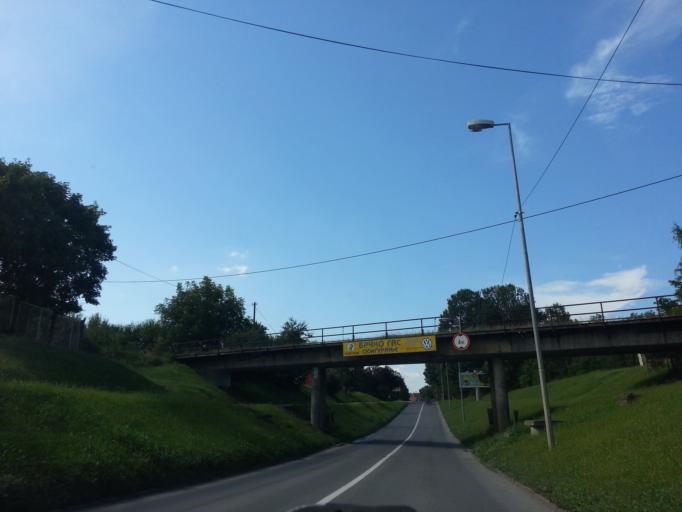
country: BA
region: Brcko
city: Brcko
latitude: 44.8650
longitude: 18.8209
